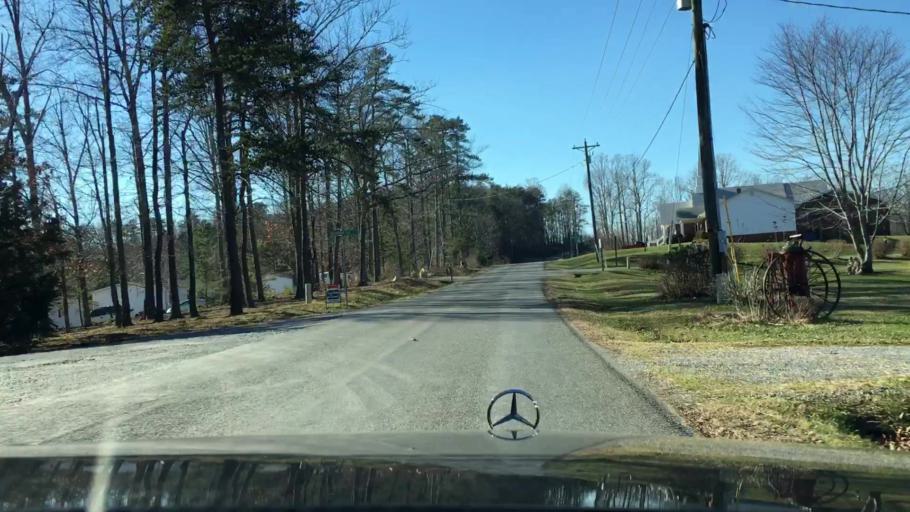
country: US
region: Virginia
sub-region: Campbell County
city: Altavista
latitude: 37.1735
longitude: -79.3365
